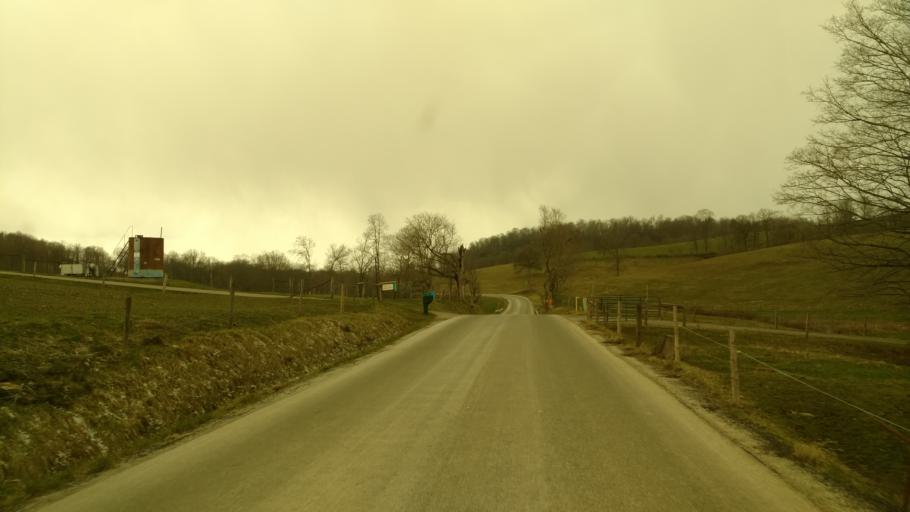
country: US
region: Ohio
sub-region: Tuscarawas County
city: Sugarcreek
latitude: 40.4465
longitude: -81.7872
